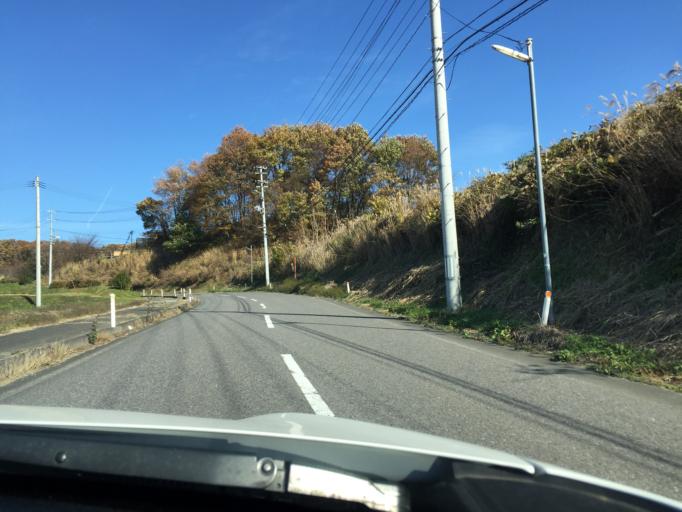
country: JP
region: Fukushima
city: Miharu
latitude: 37.4096
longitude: 140.4715
